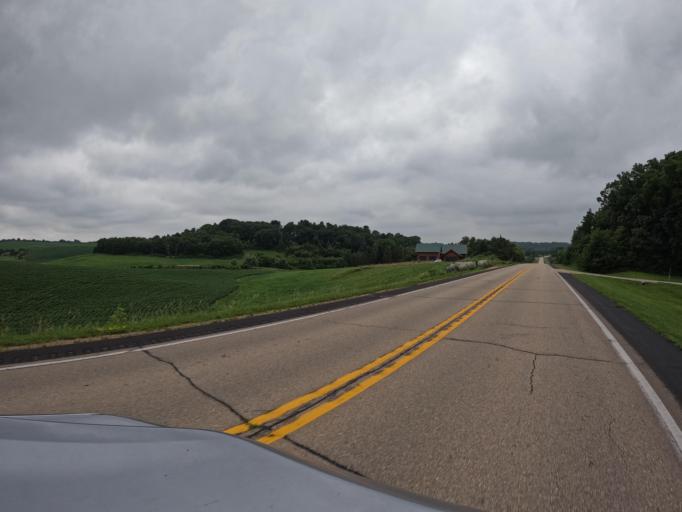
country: US
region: Illinois
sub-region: Carroll County
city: Savanna
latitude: 42.0057
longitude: -90.1845
